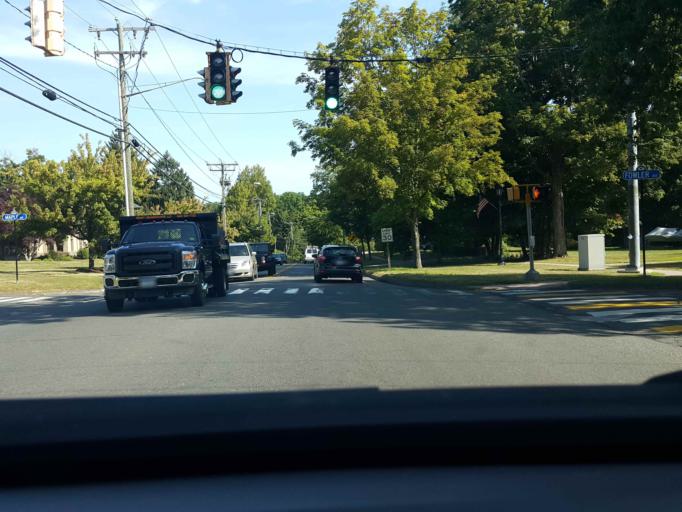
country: US
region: Connecticut
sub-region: Middlesex County
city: Durham
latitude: 41.4711
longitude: -72.6803
